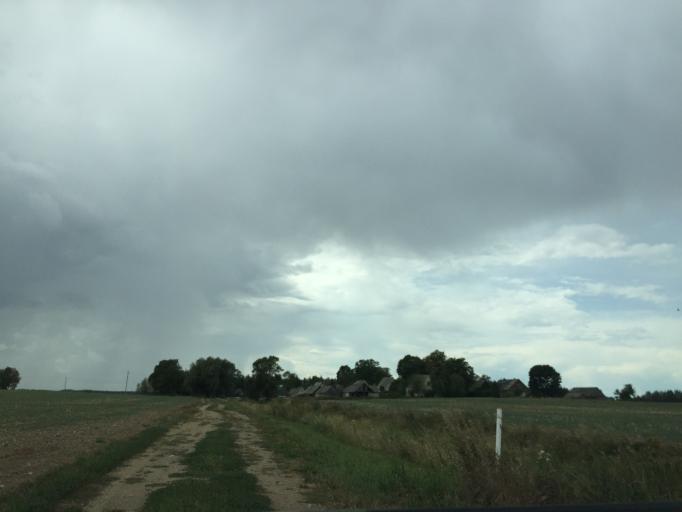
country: LT
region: Siauliu apskritis
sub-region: Joniskis
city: Joniskis
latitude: 56.2884
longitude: 23.7266
